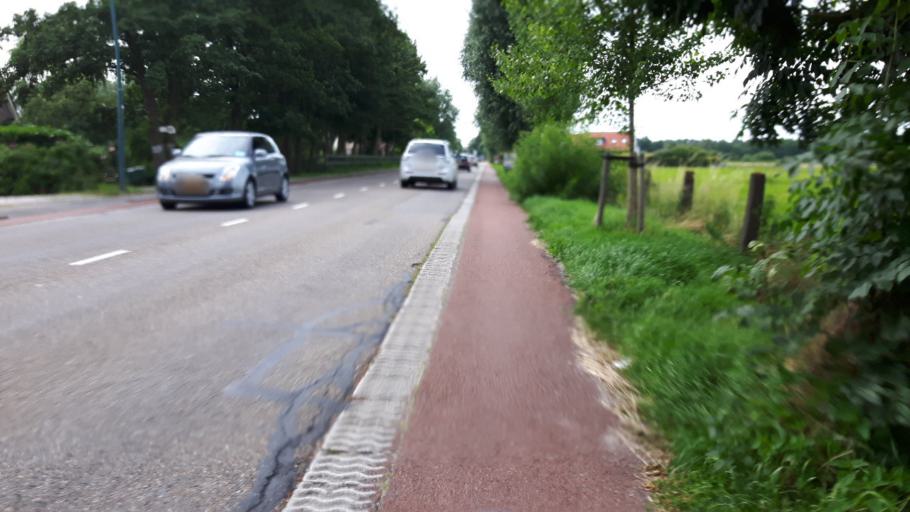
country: NL
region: North Holland
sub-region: Gemeente Wijdemeren
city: Oud-Loosdrecht
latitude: 52.2071
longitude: 5.1006
